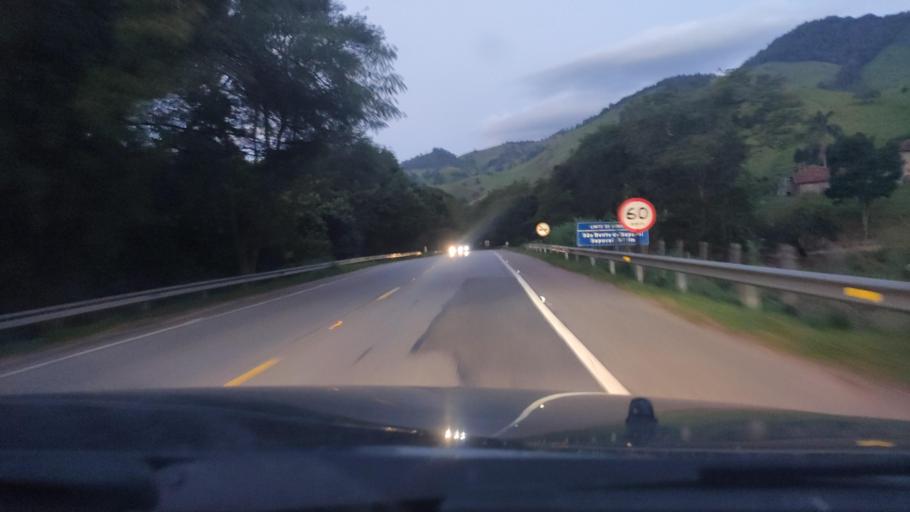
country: BR
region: Sao Paulo
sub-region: Campos Do Jordao
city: Campos do Jordao
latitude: -22.7258
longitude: -45.7290
